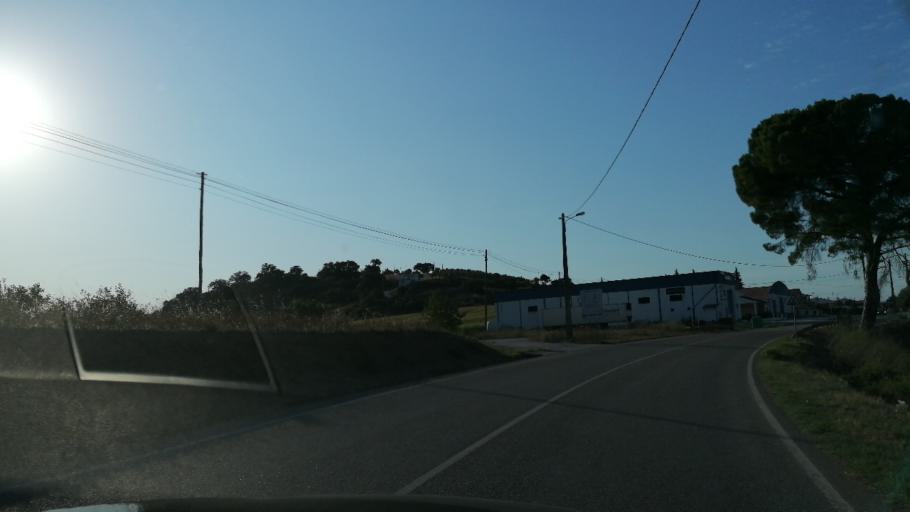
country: PT
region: Santarem
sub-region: Alcanena
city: Alcanena
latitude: 39.3616
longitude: -8.6529
